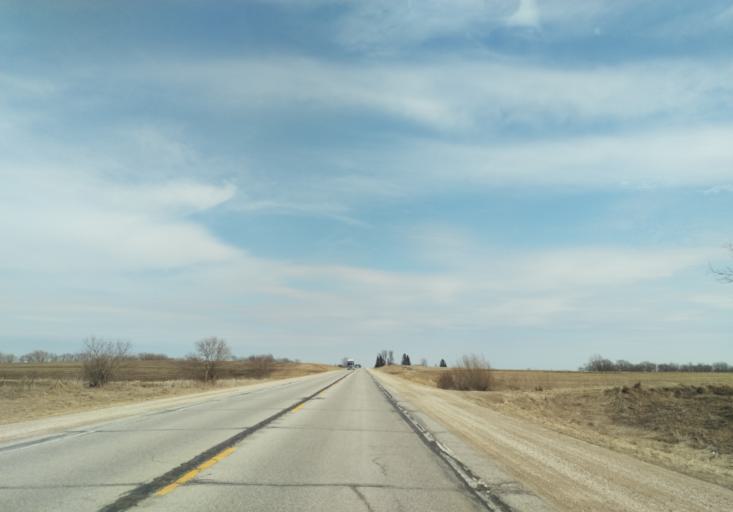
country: US
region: Iowa
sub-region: Allamakee County
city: Waukon
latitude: 43.2405
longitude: -91.6019
